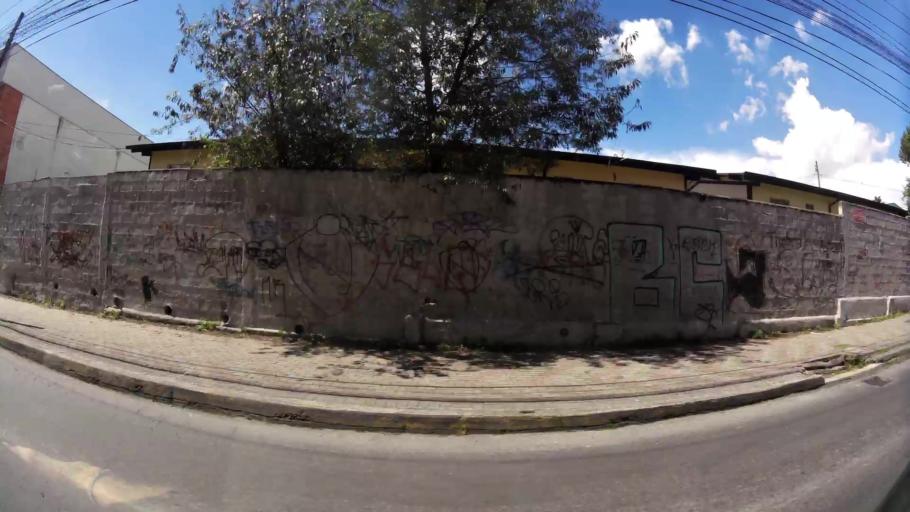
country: EC
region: Pichincha
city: Quito
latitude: -0.2655
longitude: -78.5258
